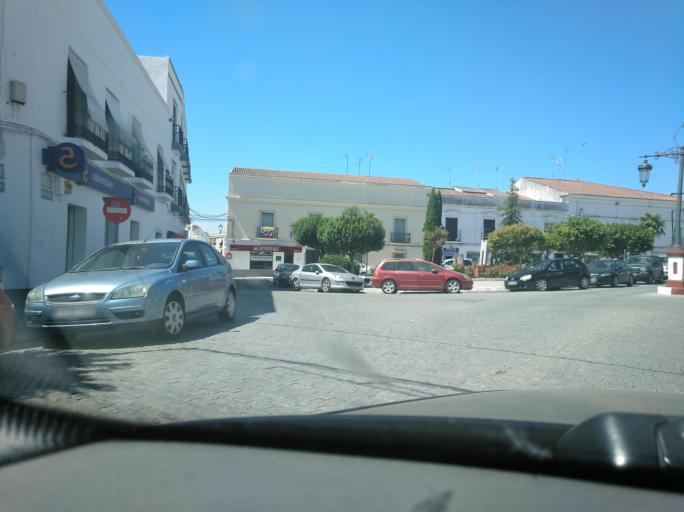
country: ES
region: Extremadura
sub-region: Provincia de Badajoz
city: Olivenza
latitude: 38.6835
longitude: -7.1001
